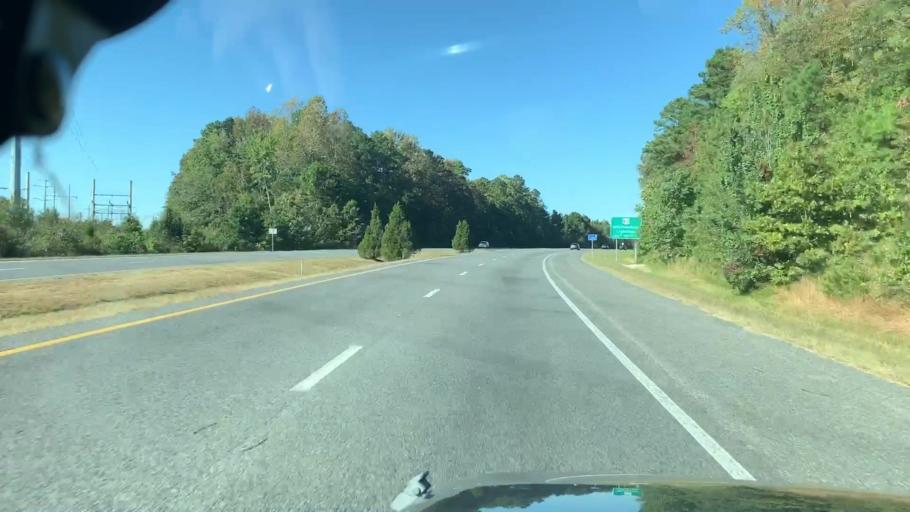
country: US
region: Virginia
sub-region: James City County
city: Williamsburg
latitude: 37.3264
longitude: -76.7554
